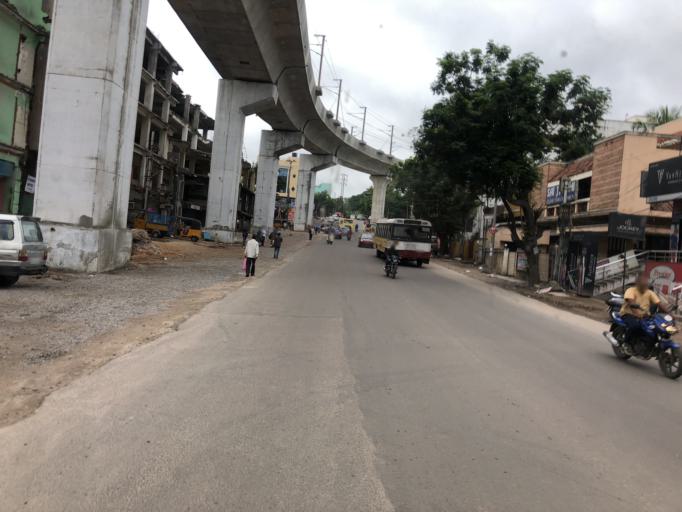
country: IN
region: Telangana
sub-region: Rangareddi
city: Kukatpalli
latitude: 17.4311
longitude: 78.4257
